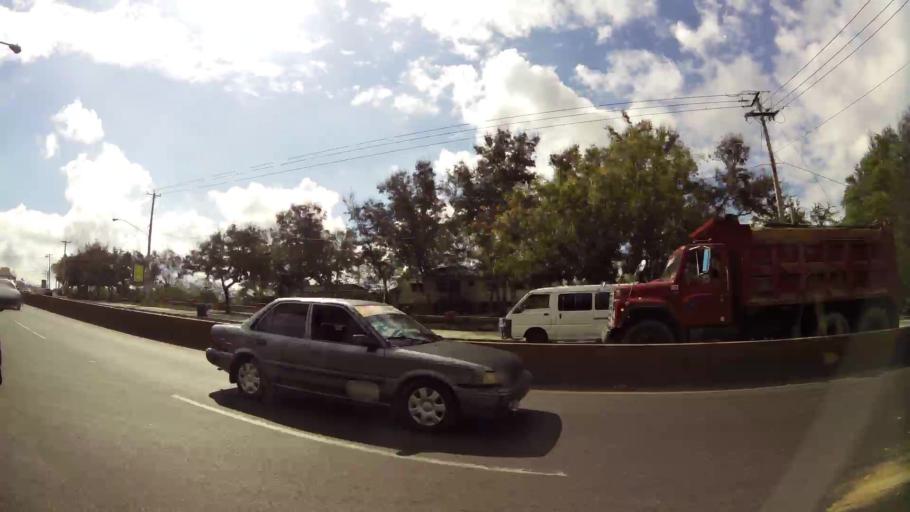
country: DO
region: Santiago
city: Santiago de los Caballeros
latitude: 19.4493
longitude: -70.7076
